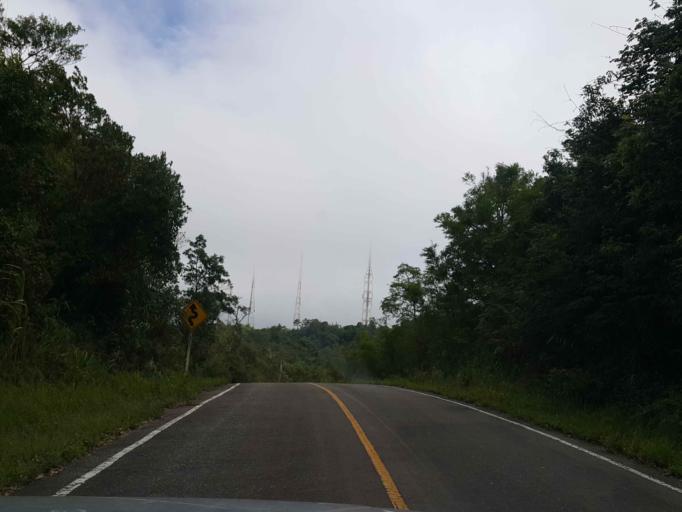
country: TH
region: Tak
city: Tak
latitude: 16.7862
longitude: 98.9247
